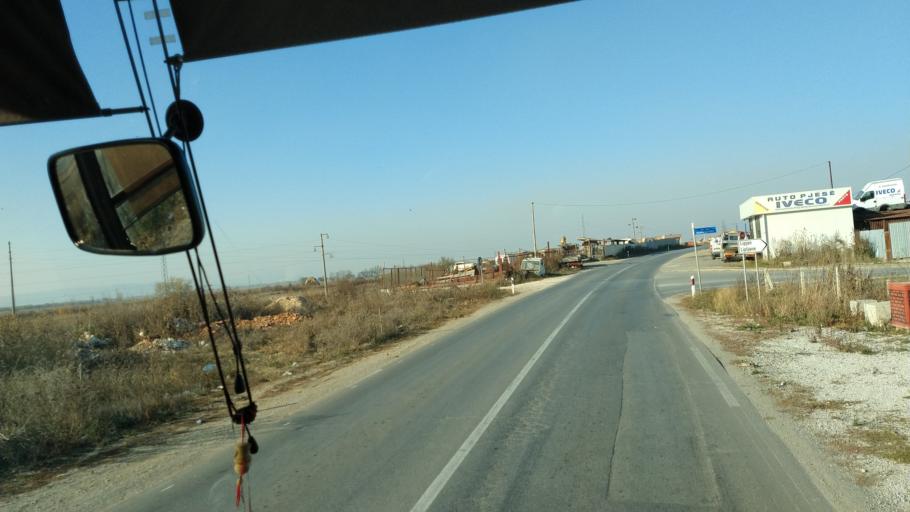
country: XK
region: Pristina
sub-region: Lipjan
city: Lipljan
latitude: 42.5252
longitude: 21.1108
